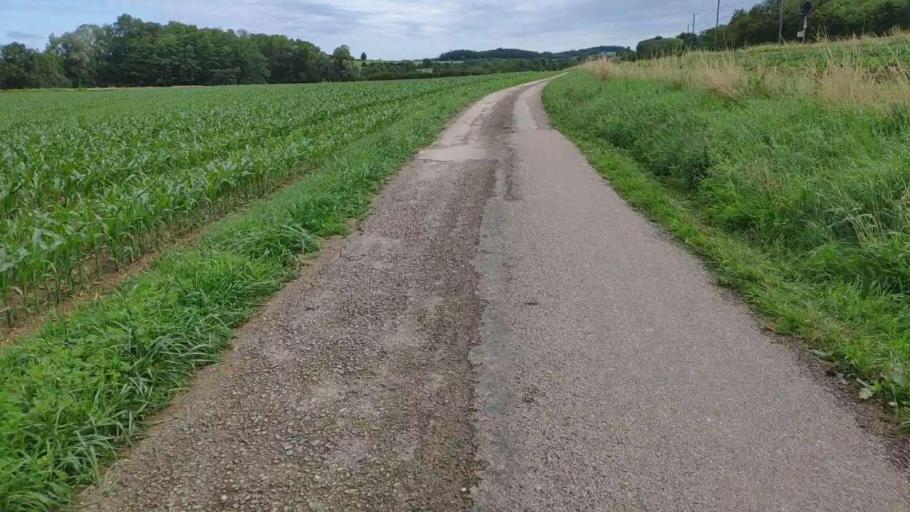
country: FR
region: Franche-Comte
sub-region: Departement du Jura
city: Poligny
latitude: 46.8072
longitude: 5.6061
